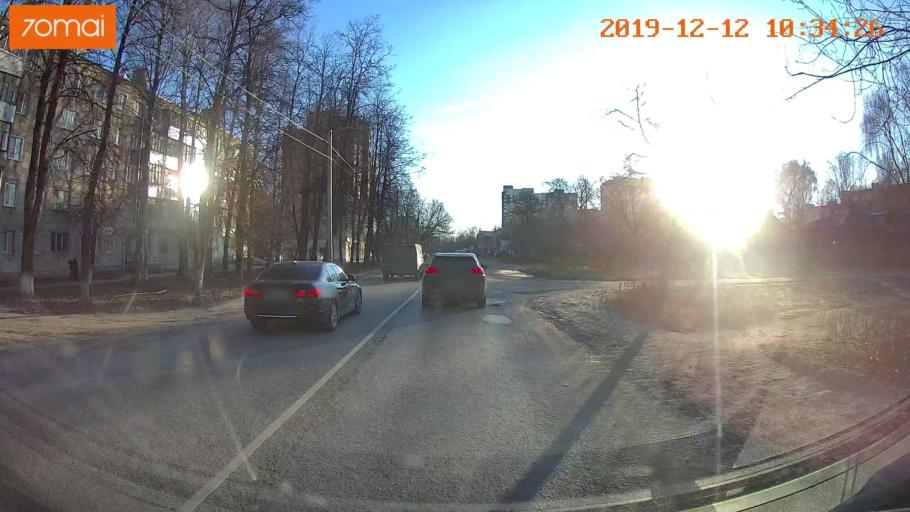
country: RU
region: Ivanovo
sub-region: Gorod Ivanovo
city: Ivanovo
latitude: 56.9898
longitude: 40.9735
